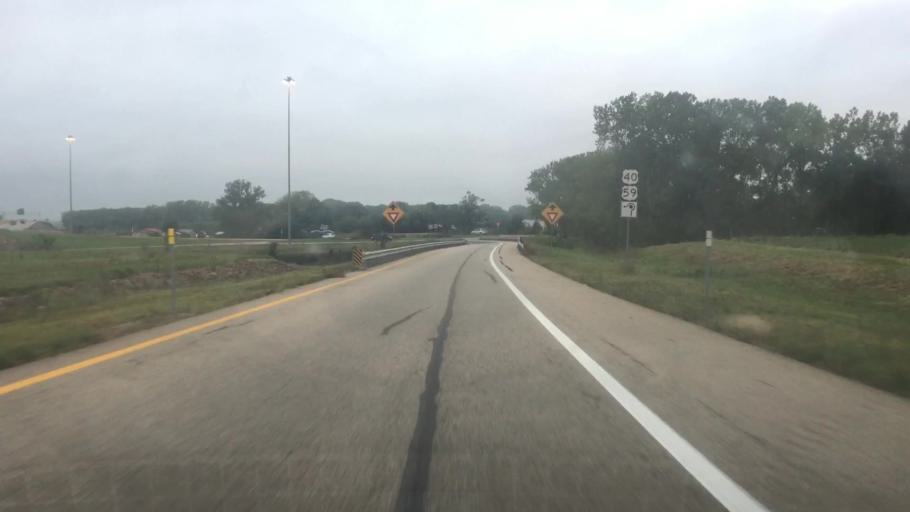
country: US
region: Kansas
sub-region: Douglas County
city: Lawrence
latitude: 38.9944
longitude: -95.2272
